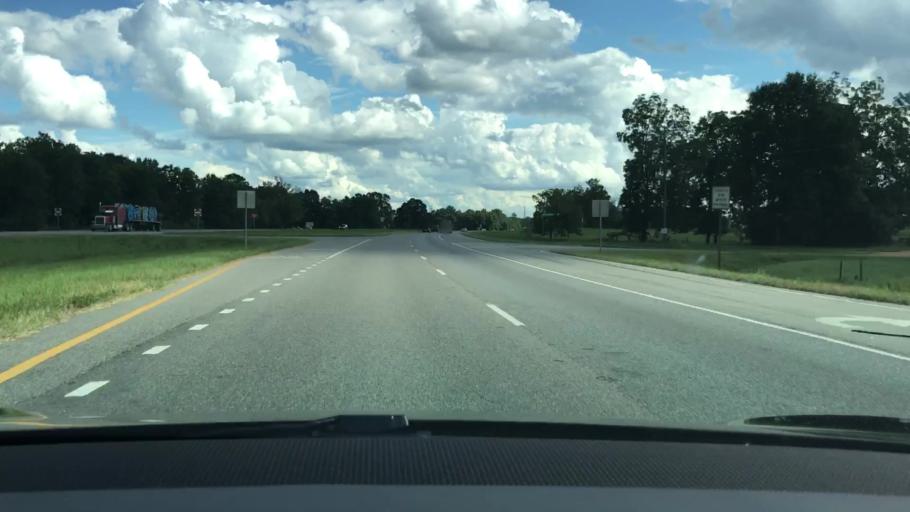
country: US
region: Alabama
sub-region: Montgomery County
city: Taylor
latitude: 32.0408
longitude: -86.0347
